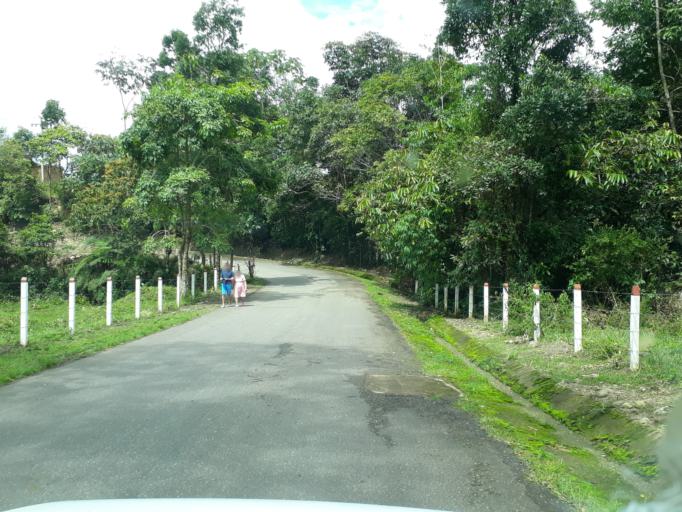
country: CO
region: Cundinamarca
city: Medina
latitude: 4.6449
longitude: -73.3214
